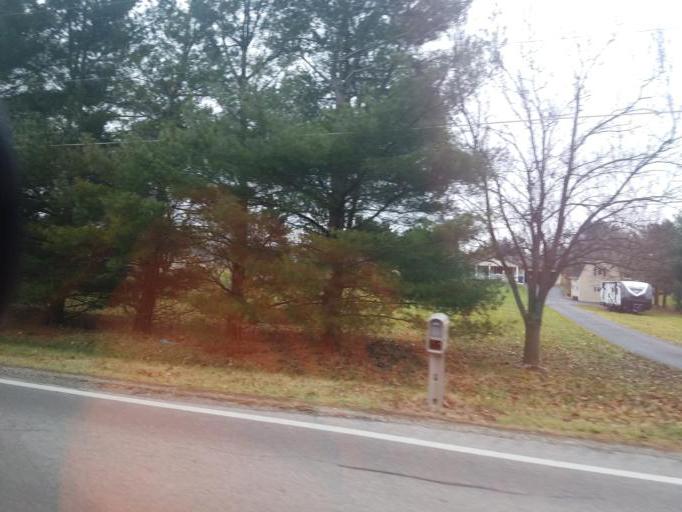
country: US
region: Ohio
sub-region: Delaware County
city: Lewis Center
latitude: 40.2165
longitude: -82.9411
